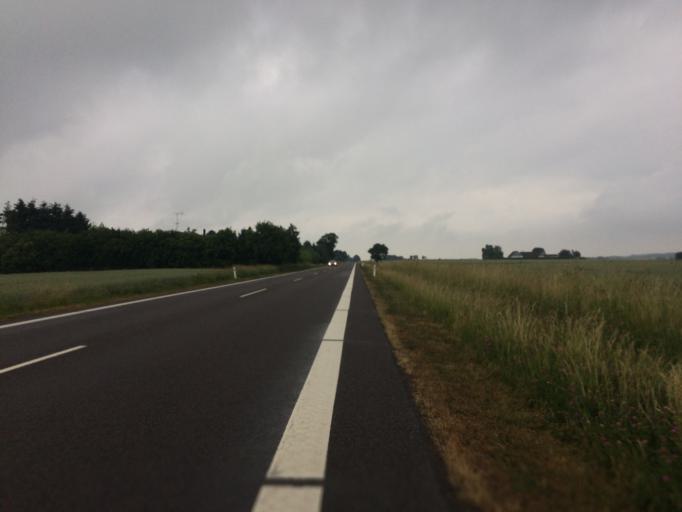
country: DK
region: Capital Region
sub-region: Bornholm Kommune
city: Akirkeby
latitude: 55.1345
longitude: 14.8397
